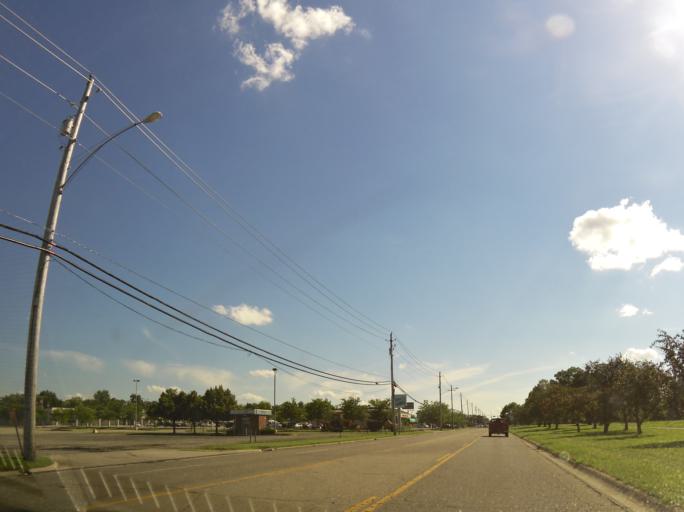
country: US
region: Ohio
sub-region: Greene County
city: Fairborn
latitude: 39.8089
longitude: -84.0276
